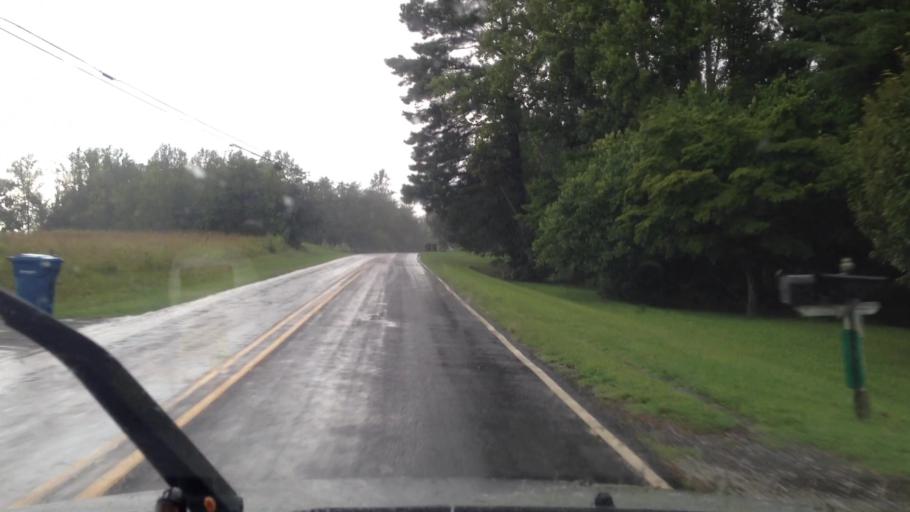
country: US
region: North Carolina
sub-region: Guilford County
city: Stokesdale
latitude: 36.2188
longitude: -80.0301
